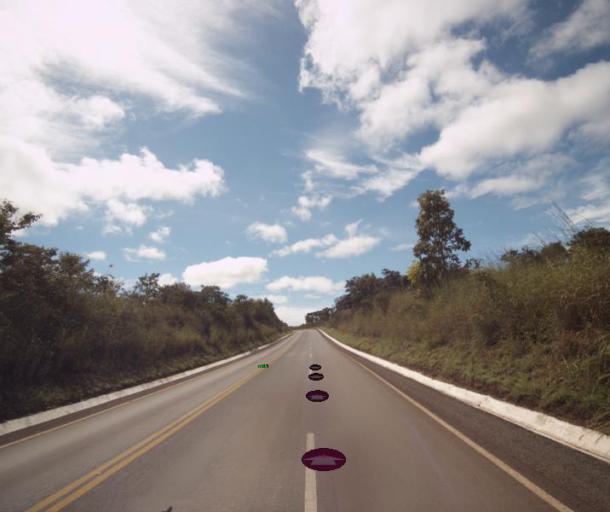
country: BR
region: Goias
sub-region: Padre Bernardo
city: Padre Bernardo
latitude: -15.2148
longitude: -48.5837
